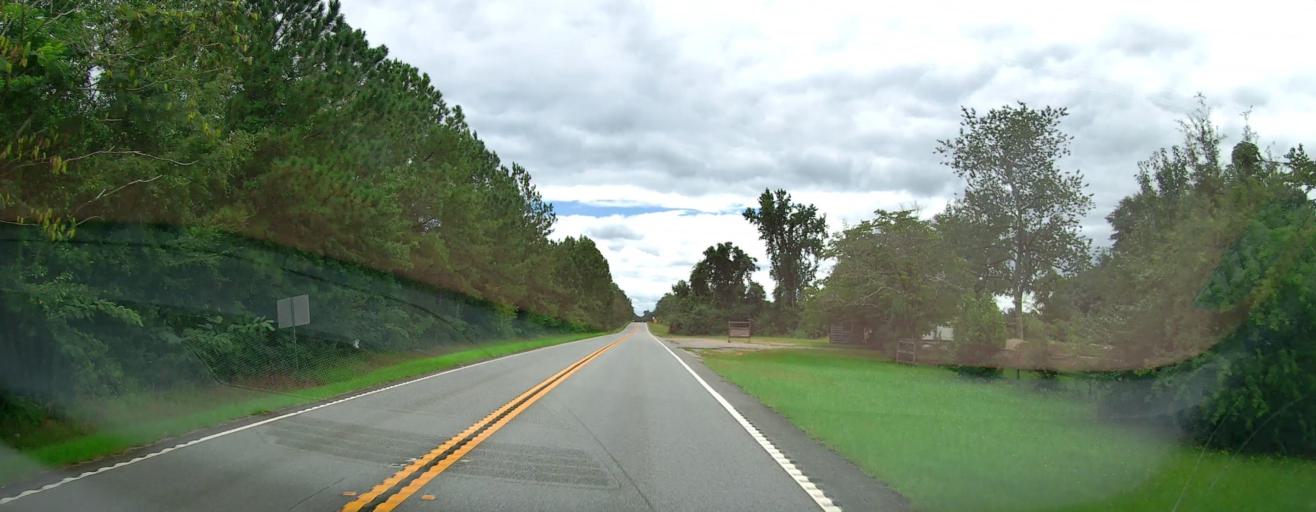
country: US
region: Georgia
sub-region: Twiggs County
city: Jeffersonville
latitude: 32.6711
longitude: -83.3285
